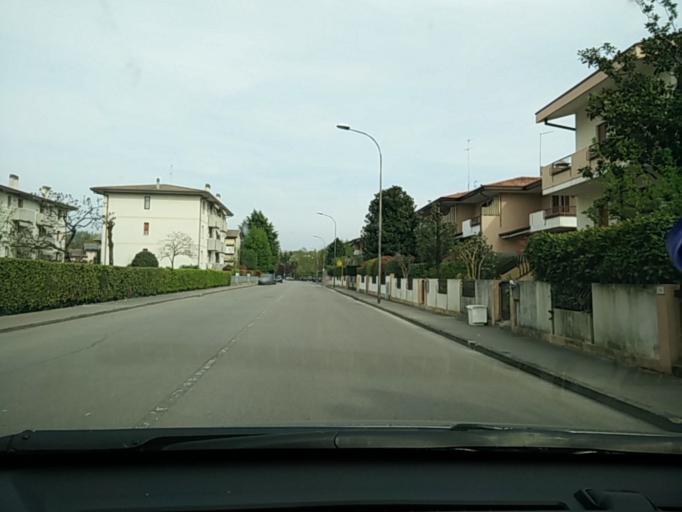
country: IT
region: Veneto
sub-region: Provincia di Venezia
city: San Dona di Piave
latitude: 45.6288
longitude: 12.5872
